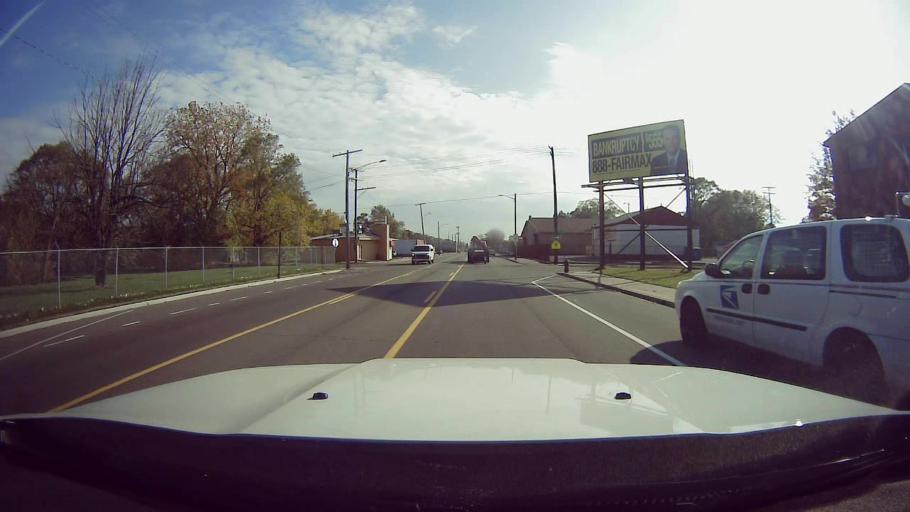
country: US
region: Michigan
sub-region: Oakland County
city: Hazel Park
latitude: 42.4382
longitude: -83.0775
